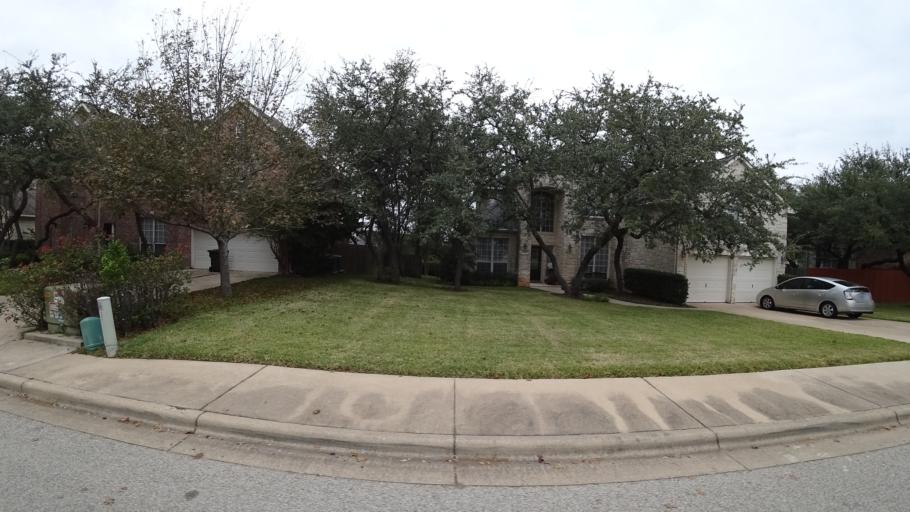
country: US
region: Texas
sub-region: Travis County
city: Bee Cave
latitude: 30.3120
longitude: -97.9315
